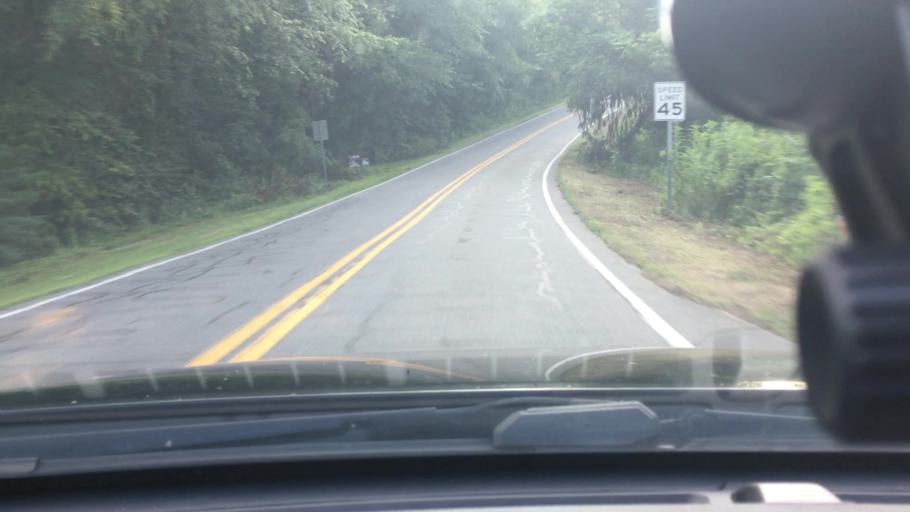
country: US
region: North Carolina
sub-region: McDowell County
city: West Marion
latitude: 35.6306
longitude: -81.9980
